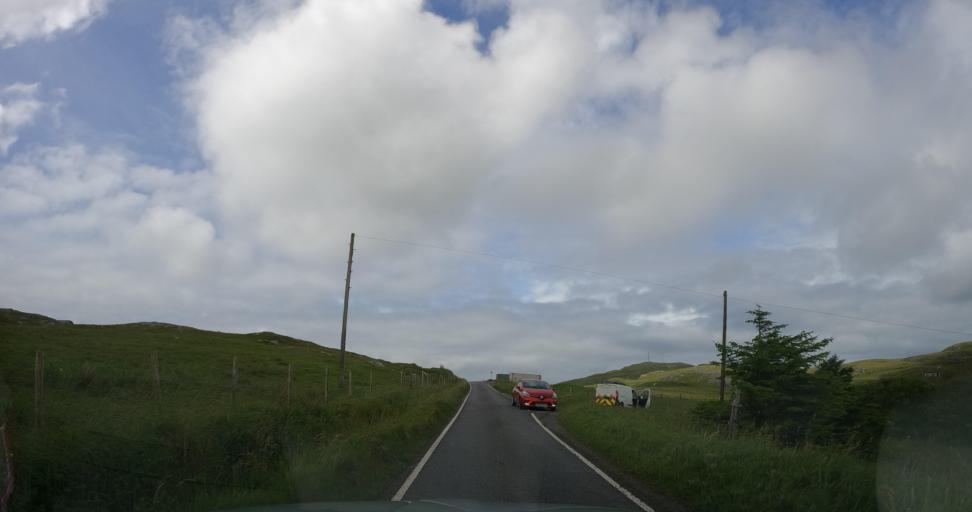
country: GB
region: Scotland
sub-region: Eilean Siar
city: Barra
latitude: 57.0023
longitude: -7.4902
